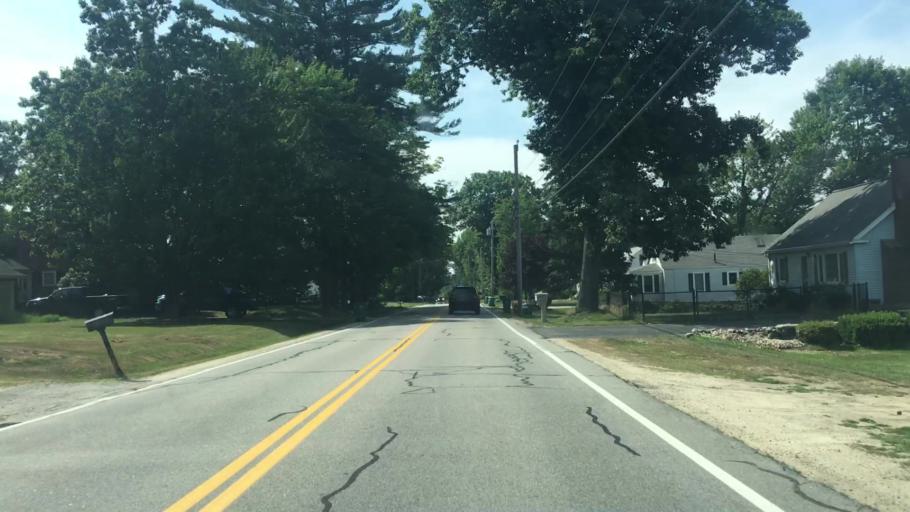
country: US
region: New Hampshire
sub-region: Strafford County
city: Rochester
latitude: 43.3197
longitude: -70.9435
